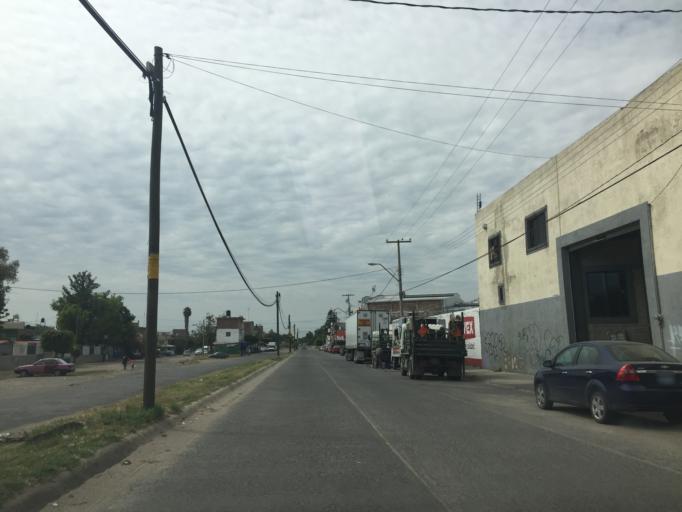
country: MX
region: Guanajuato
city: Leon
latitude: 21.1047
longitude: -101.7008
